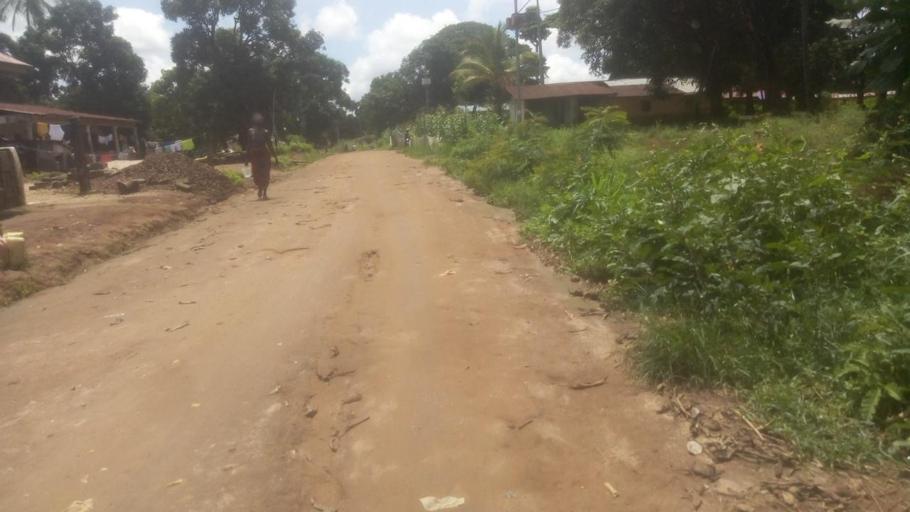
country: SL
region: Northern Province
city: Masoyila
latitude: 8.6029
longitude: -13.1997
